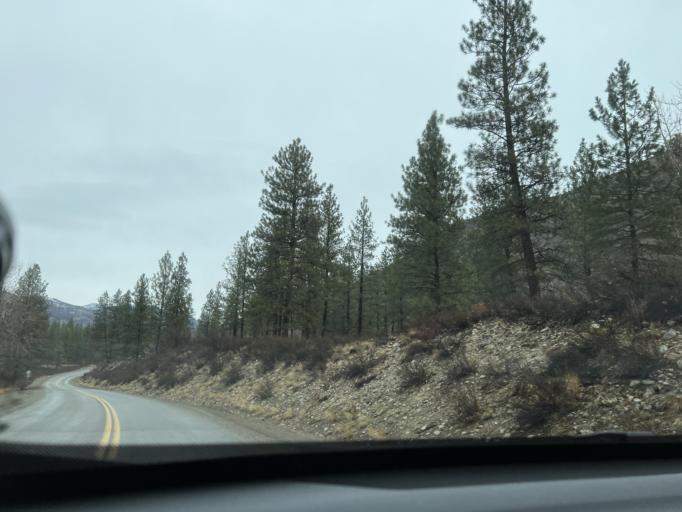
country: US
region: Washington
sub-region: Okanogan County
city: Brewster
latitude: 48.5303
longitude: -120.1801
